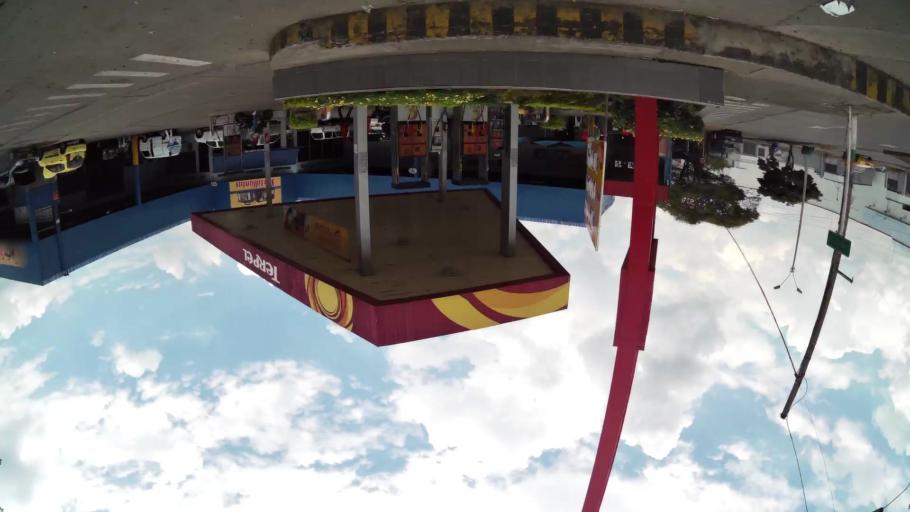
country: CO
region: Valle del Cauca
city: Cali
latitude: 3.4694
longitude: -76.5094
